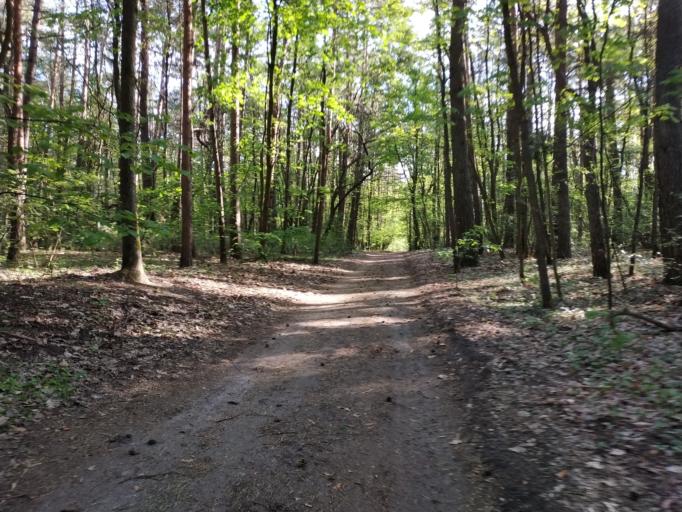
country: DE
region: Brandenburg
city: Strausberg
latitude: 52.5494
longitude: 13.8388
